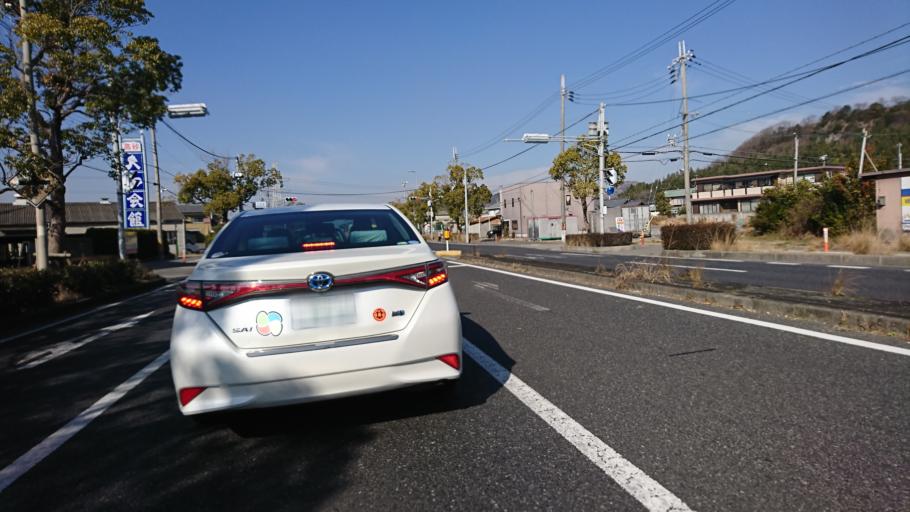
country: JP
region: Hyogo
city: Kakogawacho-honmachi
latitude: 34.7823
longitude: 134.7863
